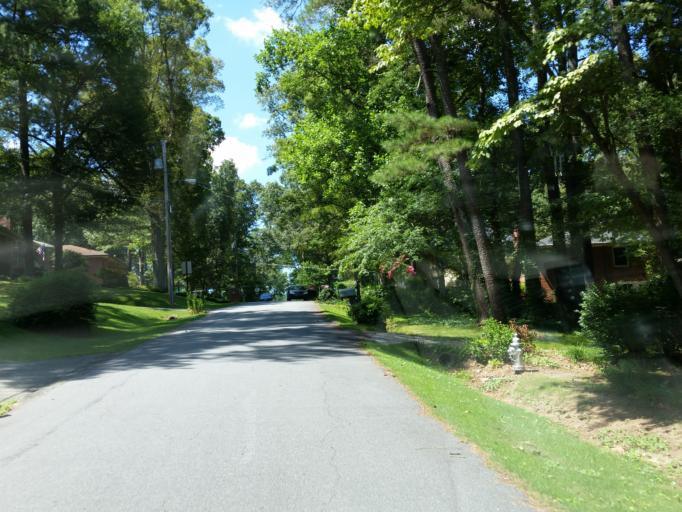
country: US
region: Georgia
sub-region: Cobb County
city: Fair Oaks
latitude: 33.9405
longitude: -84.4867
